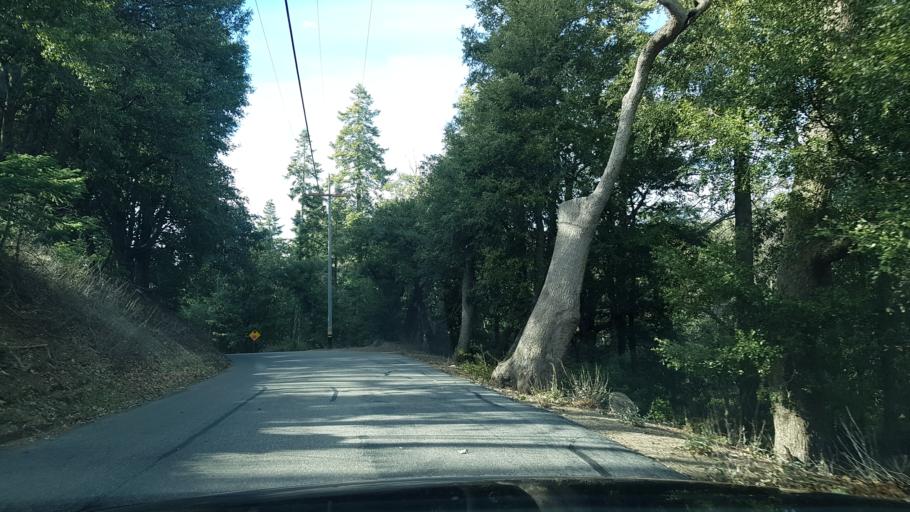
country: US
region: California
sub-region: Riverside County
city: Aguanga
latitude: 33.3315
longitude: -116.9040
